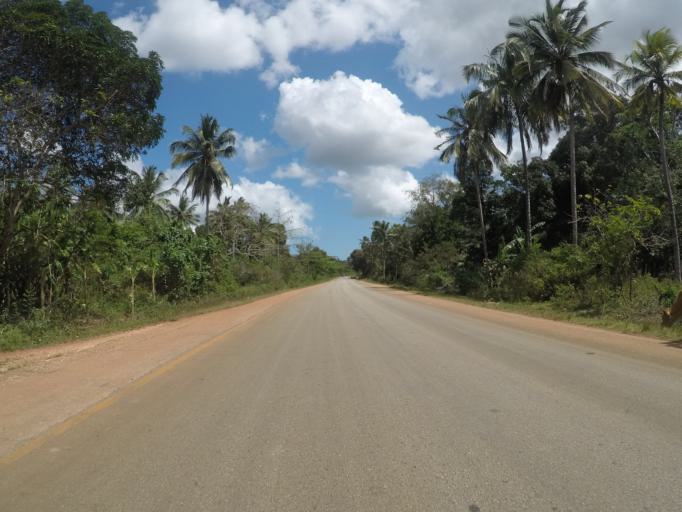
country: TZ
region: Zanzibar Central/South
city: Koani
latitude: -6.1675
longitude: 39.3303
